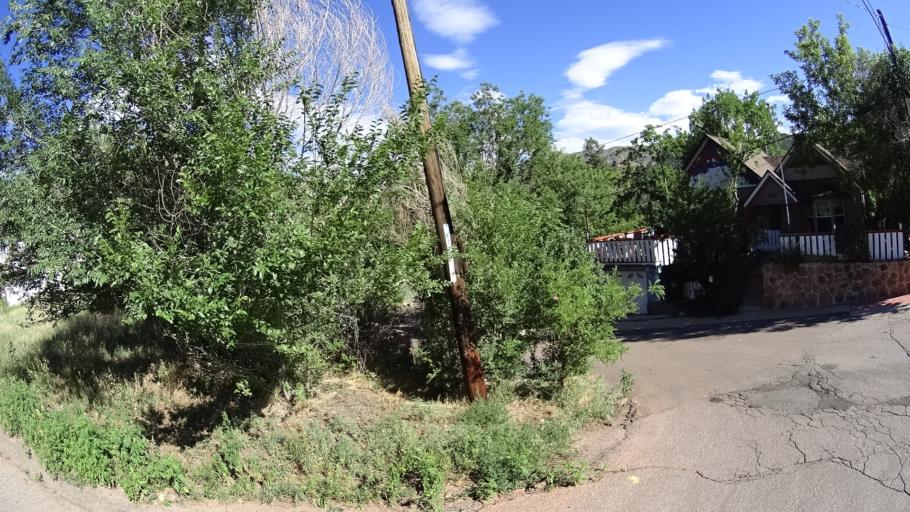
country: US
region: Colorado
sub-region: El Paso County
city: Manitou Springs
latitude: 38.8572
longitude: -104.9198
